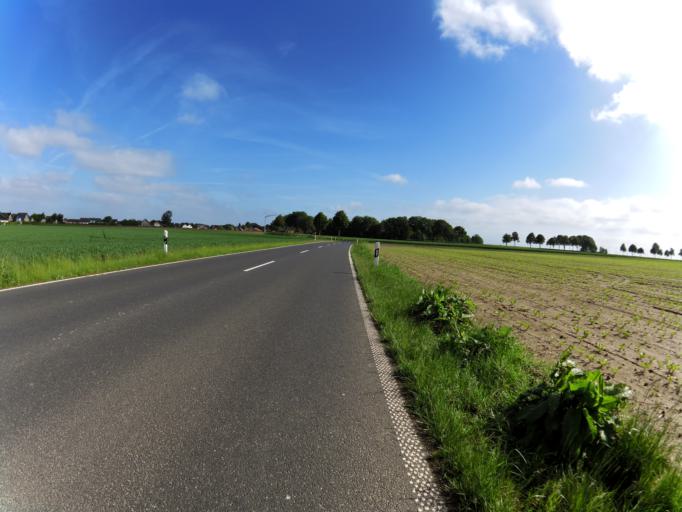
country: DE
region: North Rhine-Westphalia
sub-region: Regierungsbezirk Koln
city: Linnich
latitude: 50.9913
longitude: 6.2137
